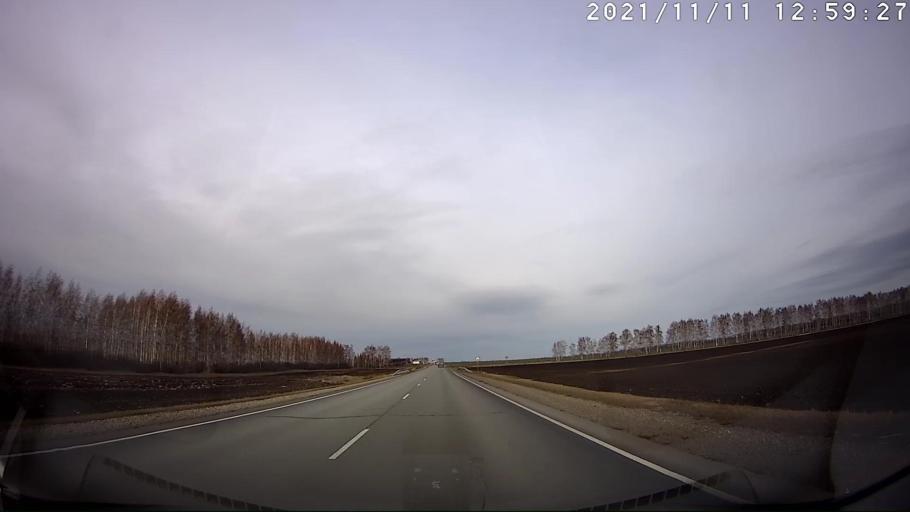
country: RU
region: Ulyanovsk
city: Isheyevka
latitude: 54.3566
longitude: 48.2118
